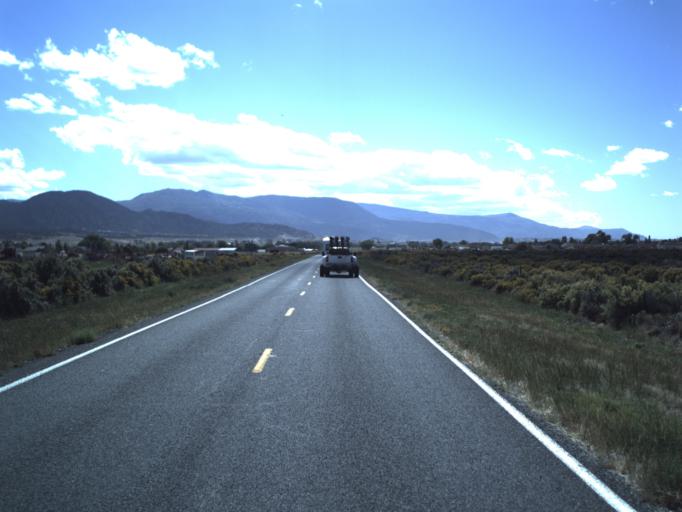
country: US
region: Utah
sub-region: Iron County
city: Enoch
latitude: 37.7744
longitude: -113.0553
